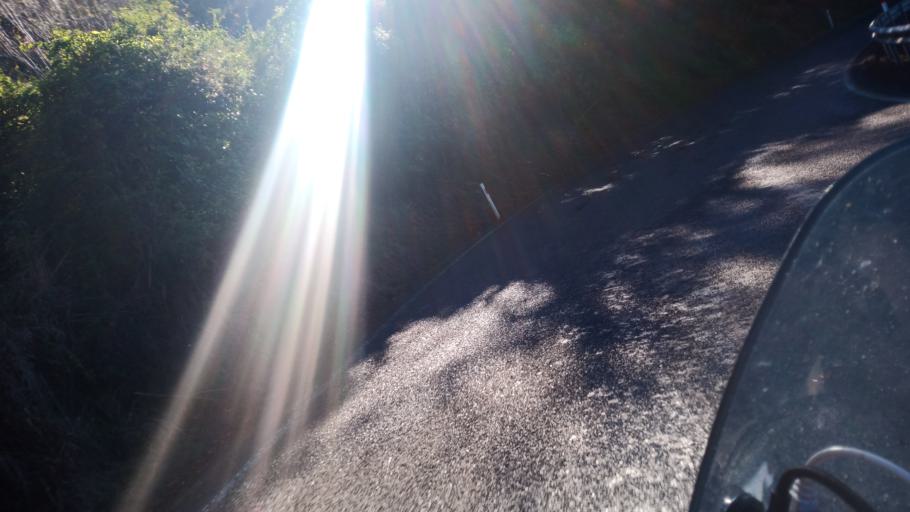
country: NZ
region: Hawke's Bay
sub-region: Wairoa District
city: Wairoa
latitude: -38.8703
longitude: 177.2126
